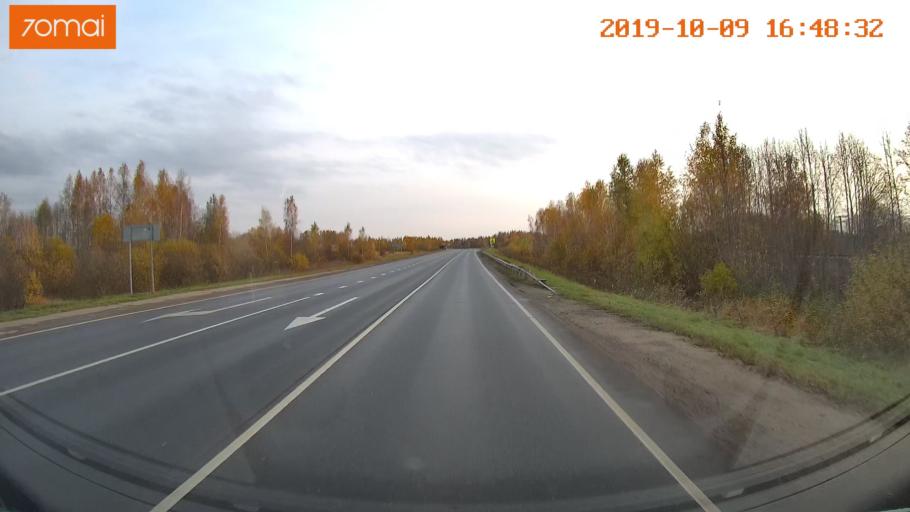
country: RU
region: Kostroma
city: Volgorechensk
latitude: 57.4272
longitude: 41.1904
